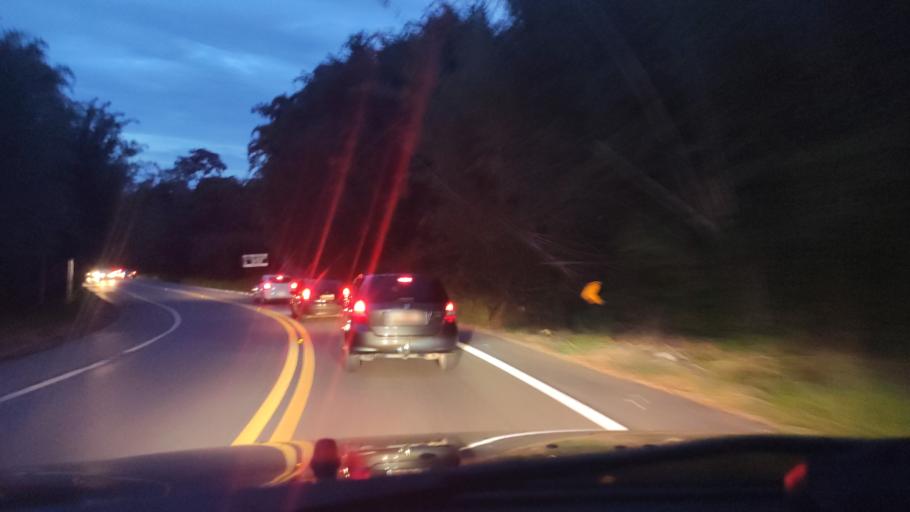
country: BR
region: Sao Paulo
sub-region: Socorro
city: Socorro
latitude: -22.5628
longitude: -46.5496
